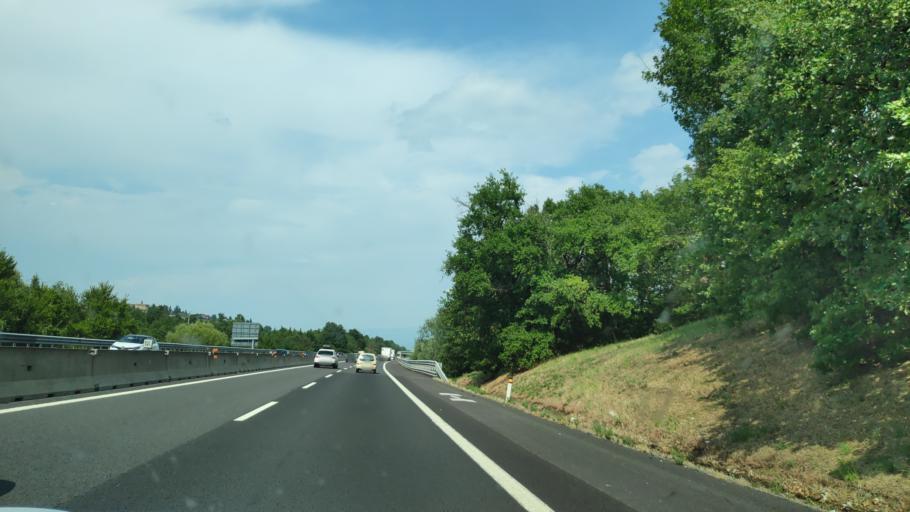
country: IT
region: Tuscany
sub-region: Province of Arezzo
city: Badia al Pino
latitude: 43.4120
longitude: 11.7664
